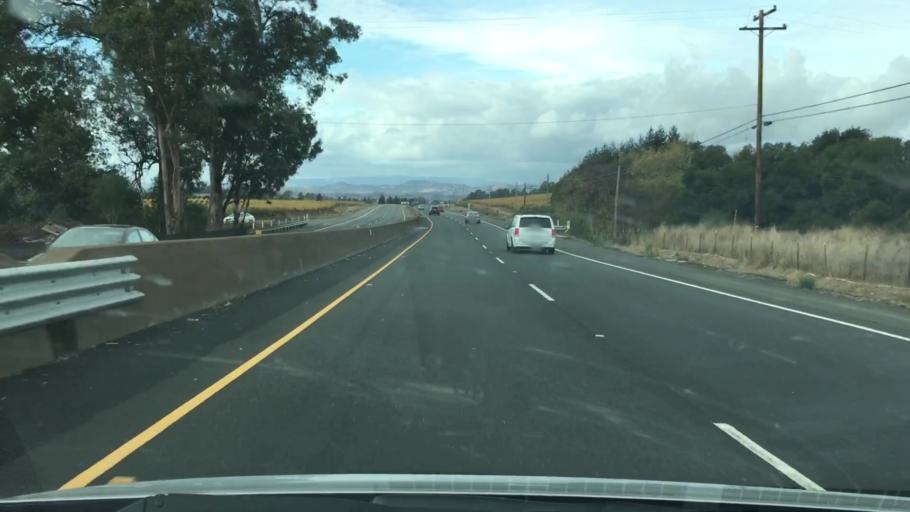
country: US
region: California
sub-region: Napa County
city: American Canyon
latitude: 38.2165
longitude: -122.2237
